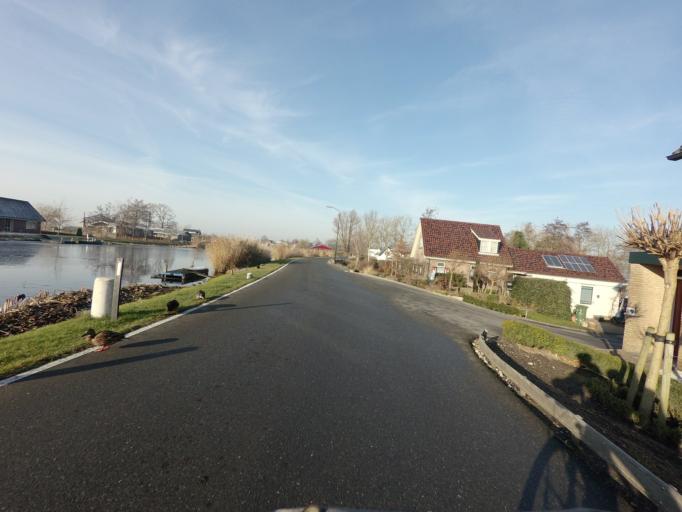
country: NL
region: Utrecht
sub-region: Gemeente De Ronde Venen
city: Mijdrecht
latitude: 52.1955
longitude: 4.8233
